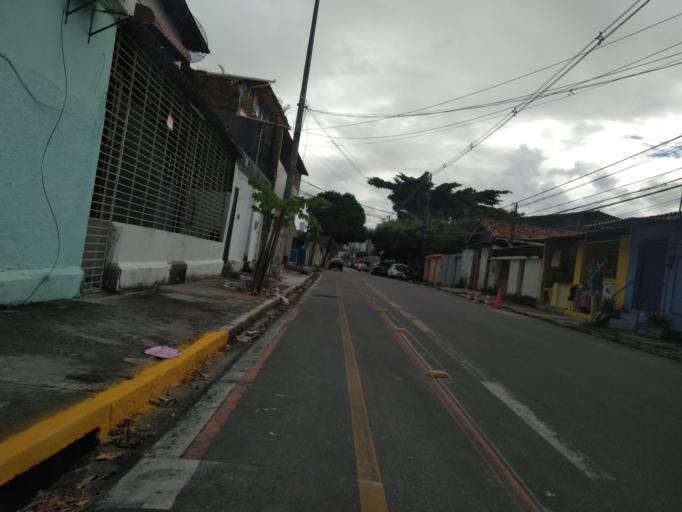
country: BR
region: Pernambuco
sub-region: Recife
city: Recife
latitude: -8.0307
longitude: -34.8817
